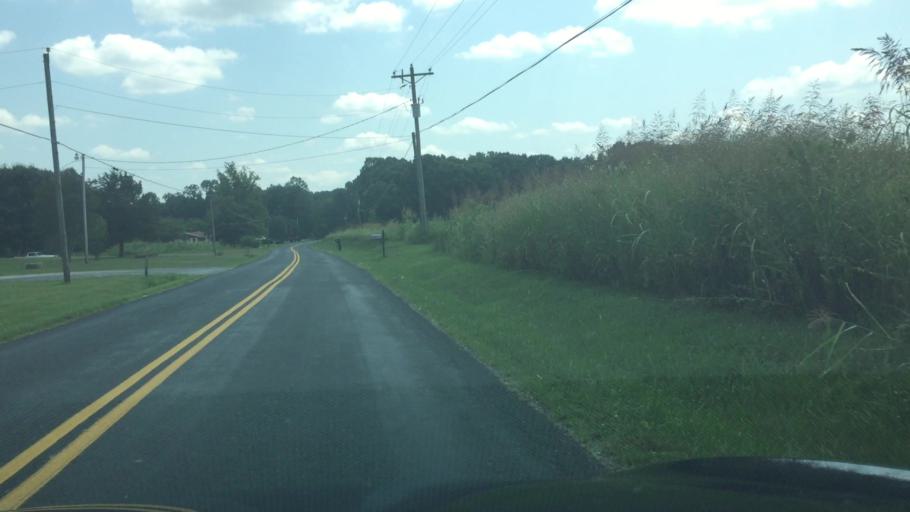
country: US
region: Virginia
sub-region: Appomattox County
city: Appomattox
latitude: 37.2926
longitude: -78.8516
